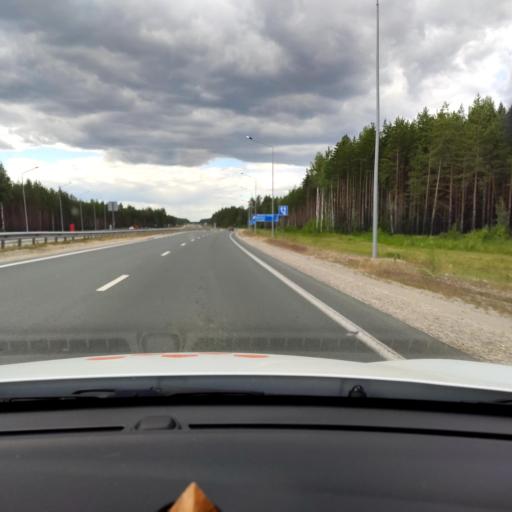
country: RU
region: Mariy-El
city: Surok
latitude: 56.4487
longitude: 48.1037
